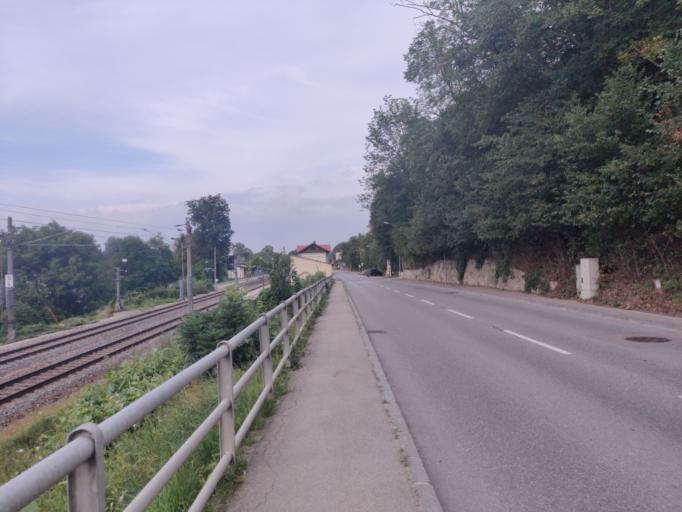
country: AT
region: Lower Austria
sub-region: Politischer Bezirk Tulln
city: Wordern
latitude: 48.3435
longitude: 16.2384
